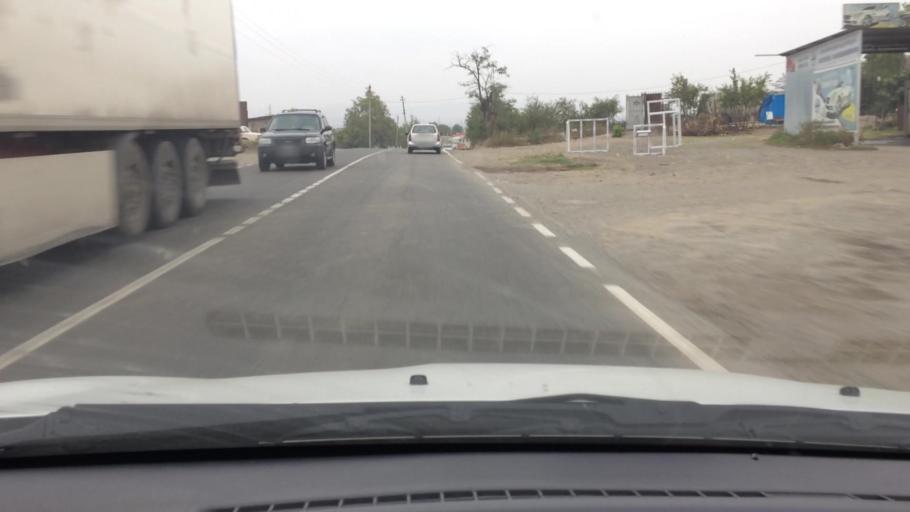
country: GE
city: Naghvarevi
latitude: 41.3719
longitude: 44.8359
